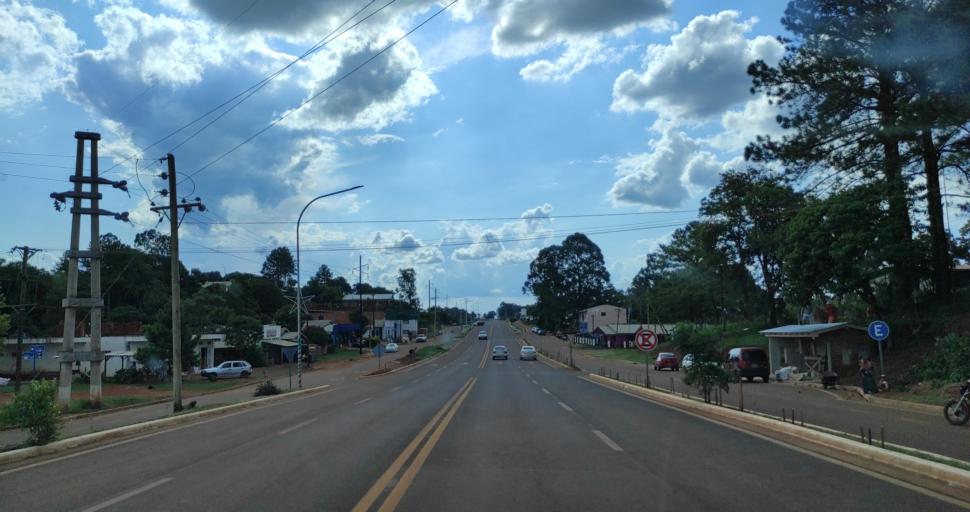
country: AR
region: Misiones
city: Bernardo de Irigoyen
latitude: -26.2944
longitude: -53.7570
